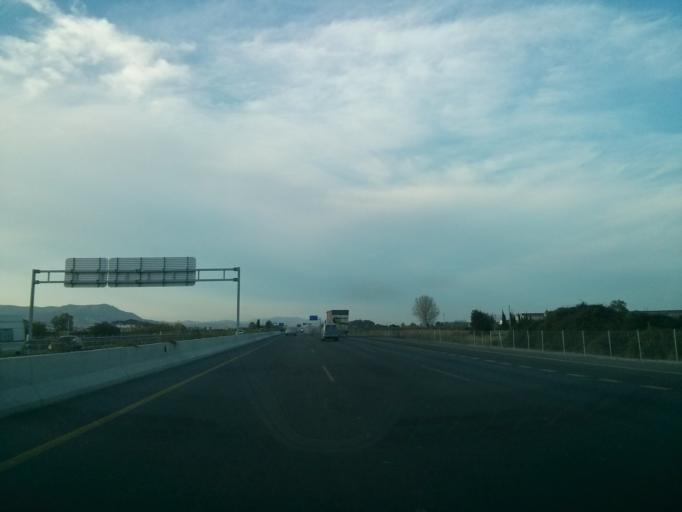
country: ES
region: Valencia
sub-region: Provincia de Valencia
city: Puig
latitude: 39.5709
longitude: -0.2956
